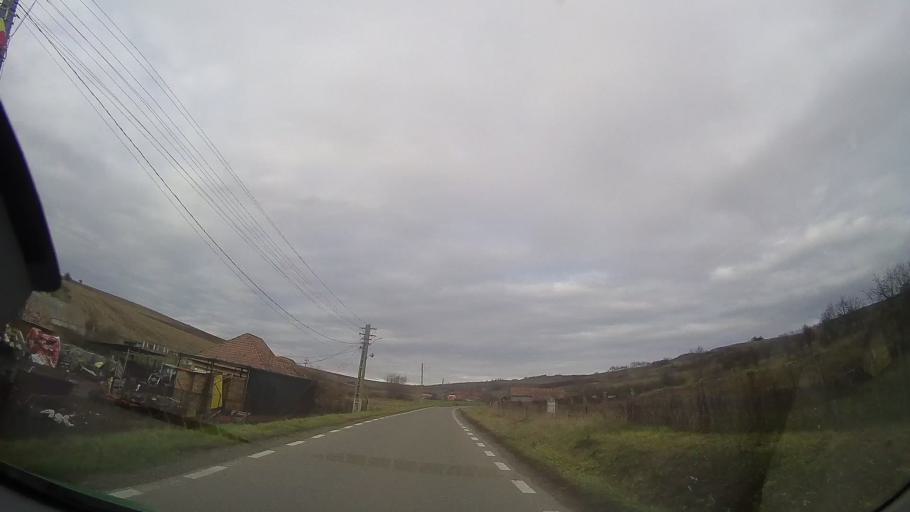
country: RO
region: Mures
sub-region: Comuna Cozma
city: Cozma
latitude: 46.8116
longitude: 24.5004
